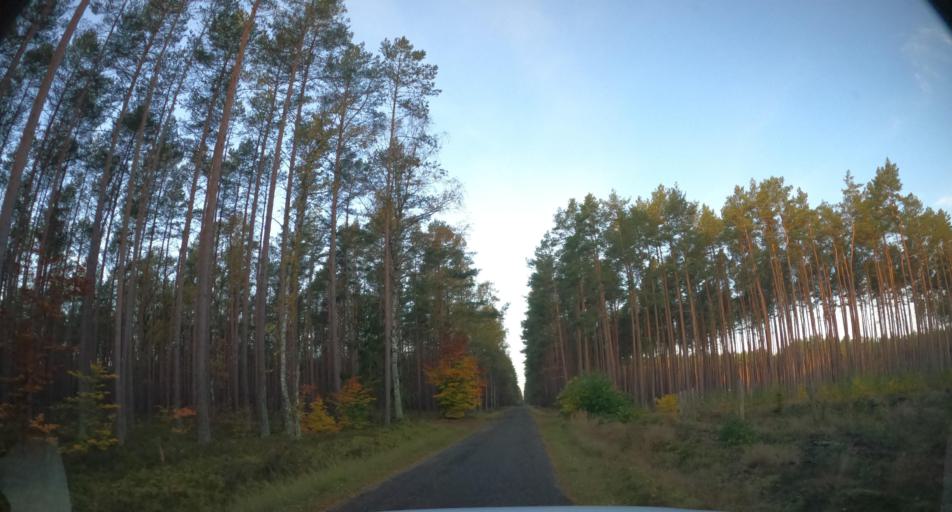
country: PL
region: West Pomeranian Voivodeship
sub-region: Powiat policki
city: Nowe Warpno
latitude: 53.6442
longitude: 14.3435
